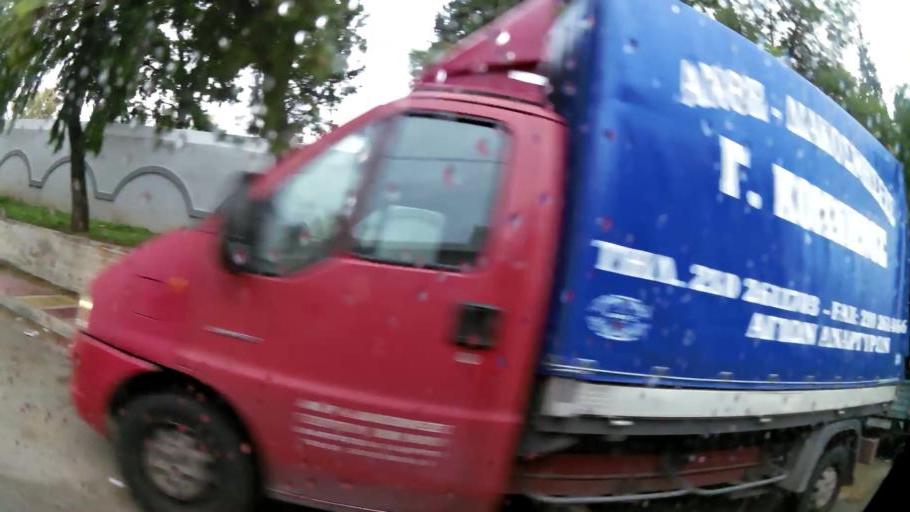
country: GR
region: Attica
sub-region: Nomarchia Athinas
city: Agioi Anargyroi
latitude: 38.0366
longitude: 23.7246
